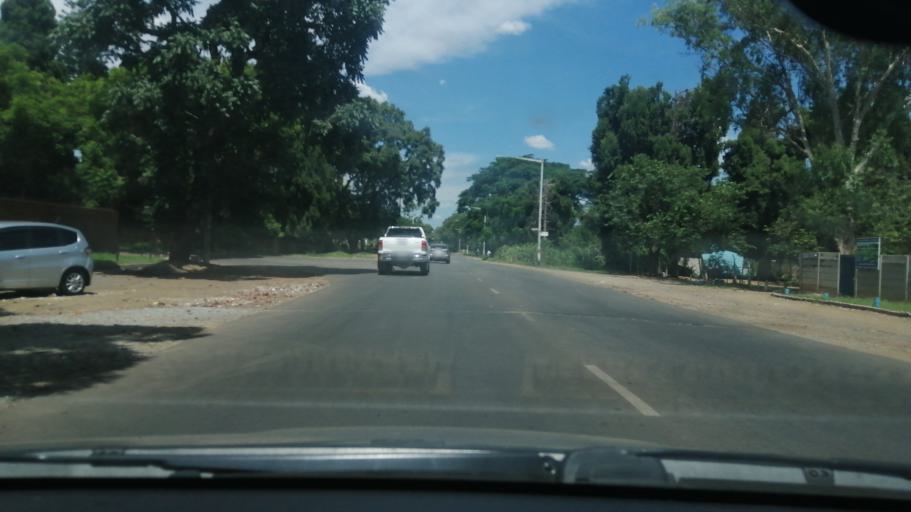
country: ZW
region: Harare
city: Harare
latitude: -17.8189
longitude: 31.0605
